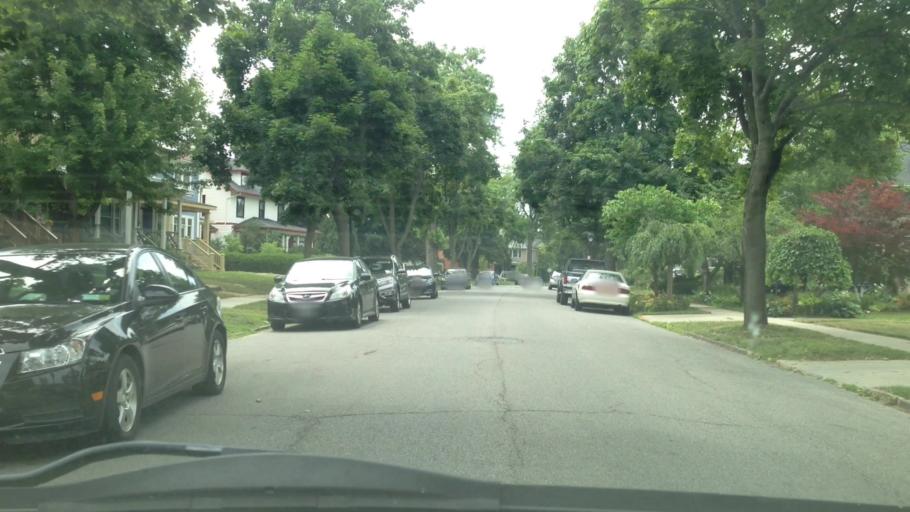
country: US
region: New York
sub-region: Erie County
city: Kenmore
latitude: 42.9399
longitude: -78.8476
